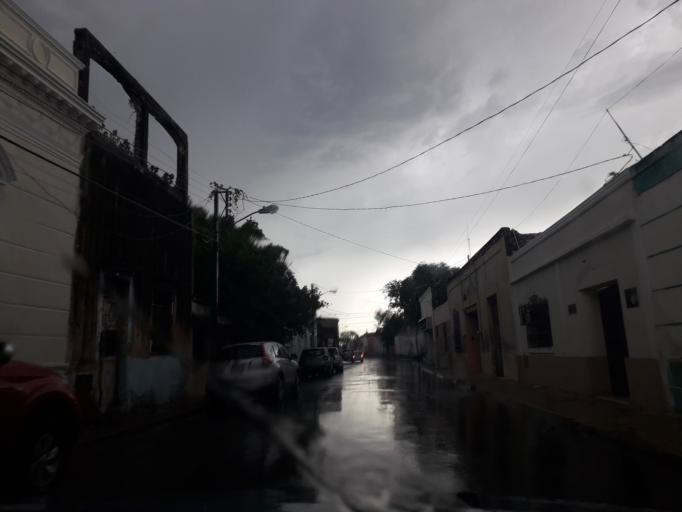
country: MX
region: Yucatan
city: Merida
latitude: 20.9716
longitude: -89.6342
